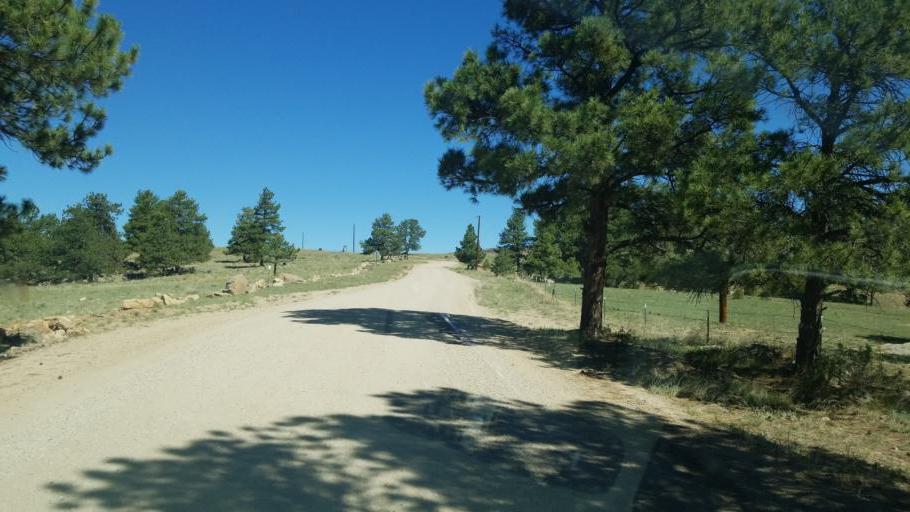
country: US
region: Colorado
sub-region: Custer County
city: Westcliffe
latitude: 38.2130
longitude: -105.4447
